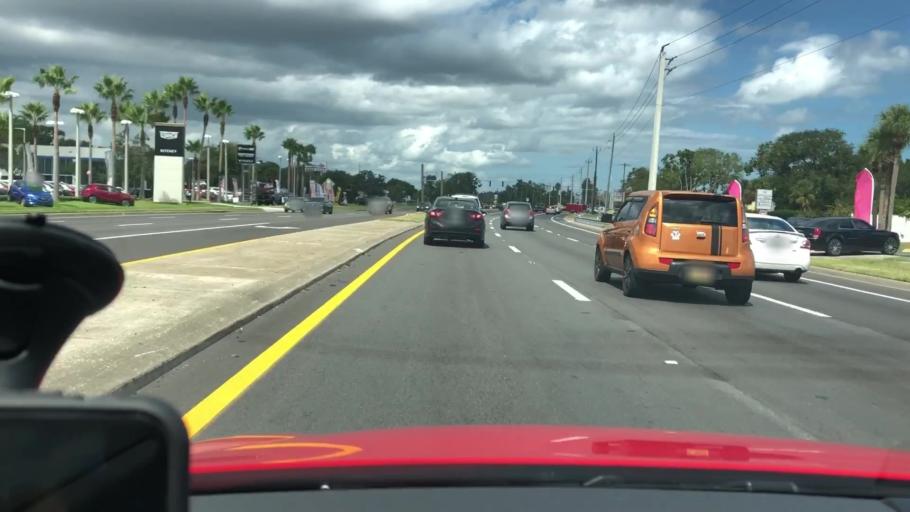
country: US
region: Florida
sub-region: Volusia County
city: Holly Hill
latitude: 29.2230
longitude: -81.0489
